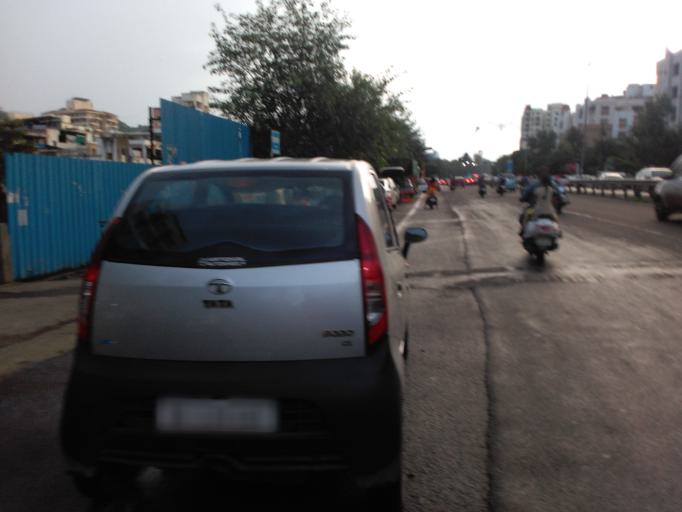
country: IN
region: Maharashtra
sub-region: Pune Division
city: Shivaji Nagar
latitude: 18.5439
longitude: 73.7836
